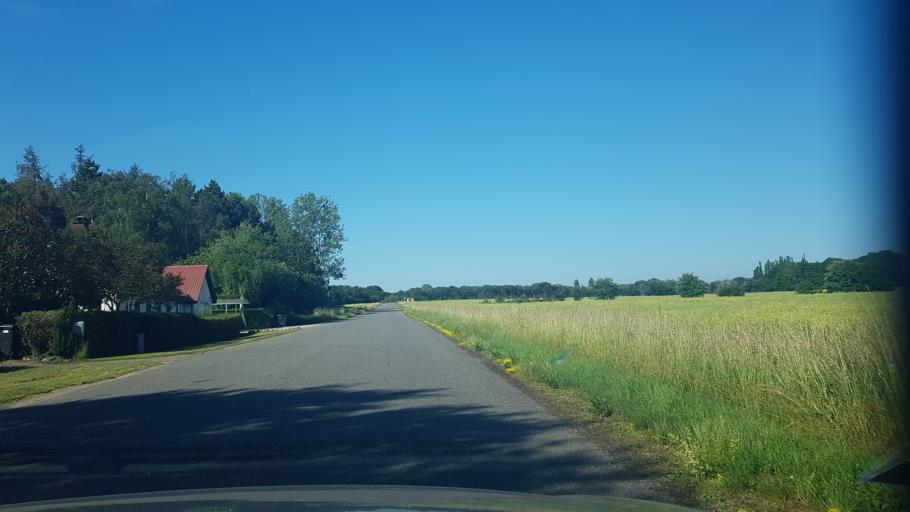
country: DK
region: Zealand
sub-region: Kalundborg Kommune
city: Svebolle
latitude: 55.6720
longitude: 11.2889
